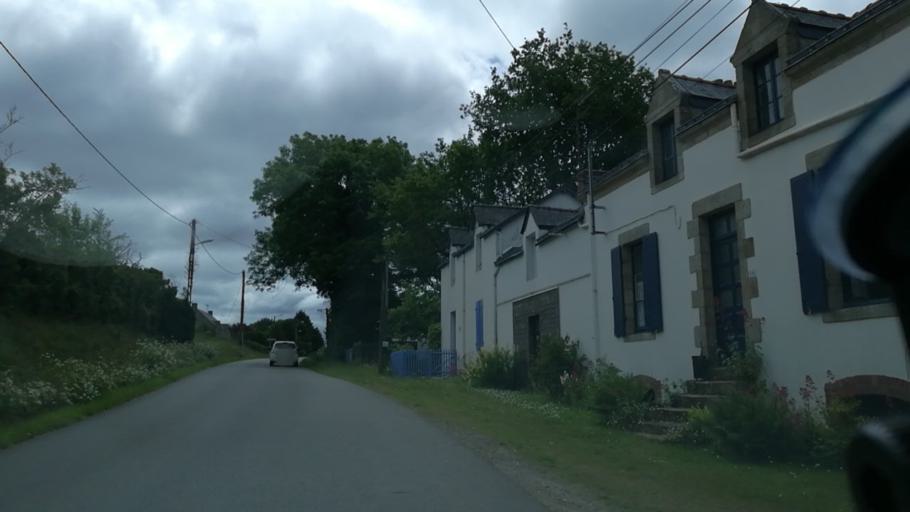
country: FR
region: Brittany
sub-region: Departement du Morbihan
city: Penestin
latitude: 47.4920
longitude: -2.4395
